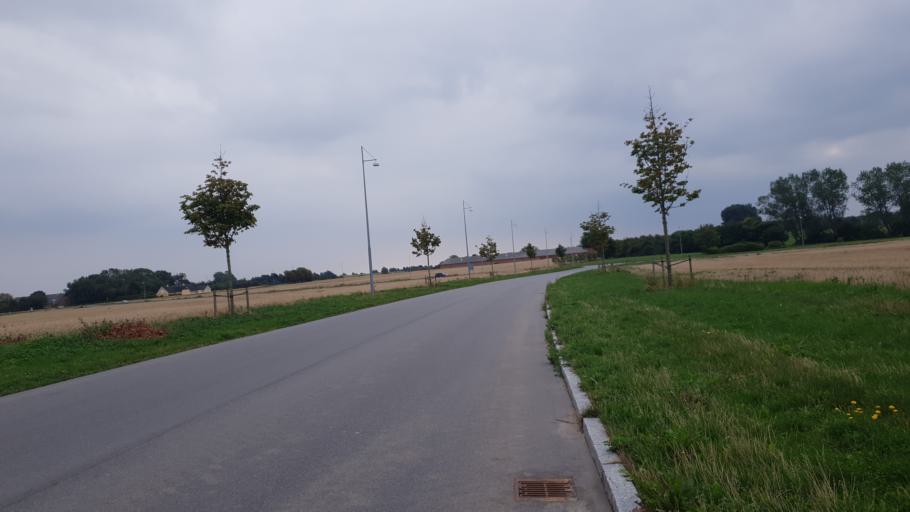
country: DK
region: South Denmark
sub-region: Middelfart Kommune
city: Strib
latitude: 55.4977
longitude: 9.7878
